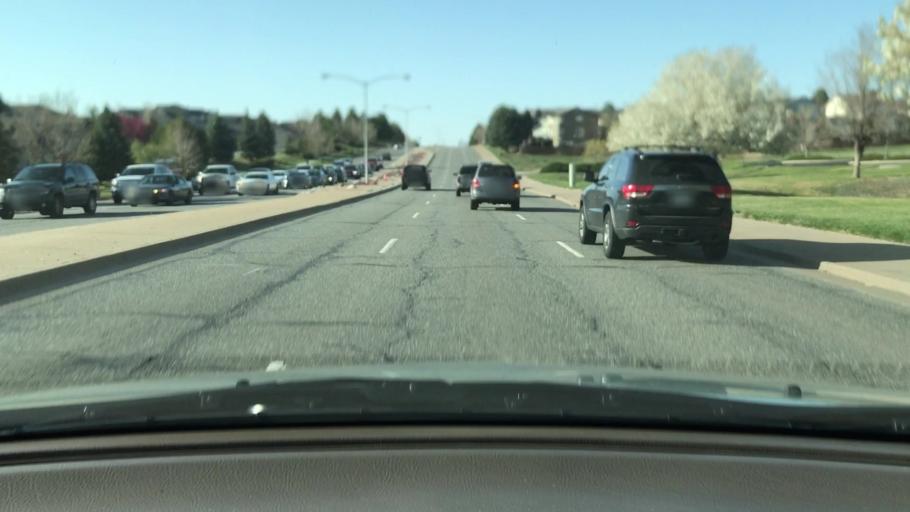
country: US
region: Colorado
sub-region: Adams County
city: Aurora
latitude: 39.6575
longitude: -104.7723
